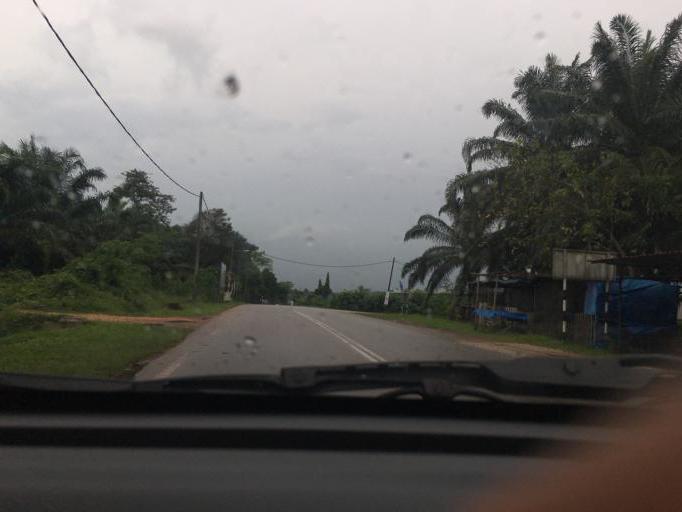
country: MY
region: Kedah
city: Bedong
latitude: 5.7020
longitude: 100.6323
